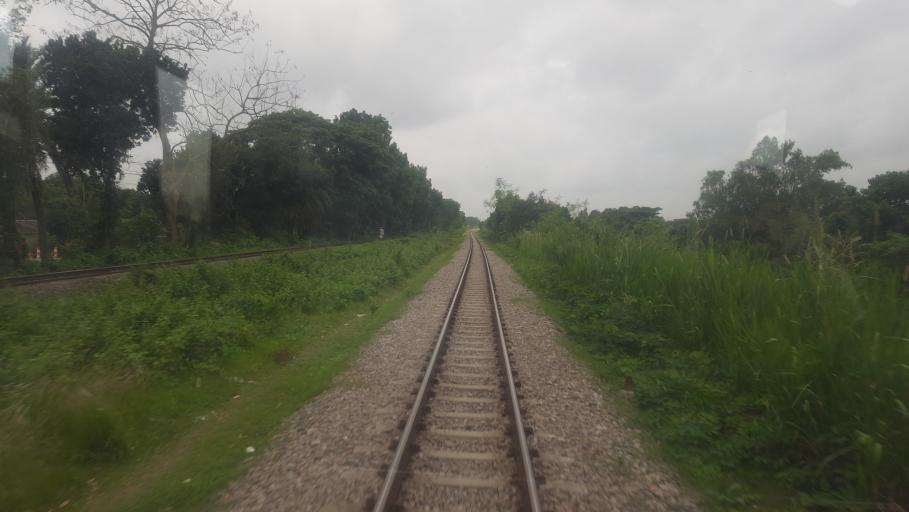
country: BD
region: Dhaka
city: Narsingdi
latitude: 23.9322
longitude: 90.7515
